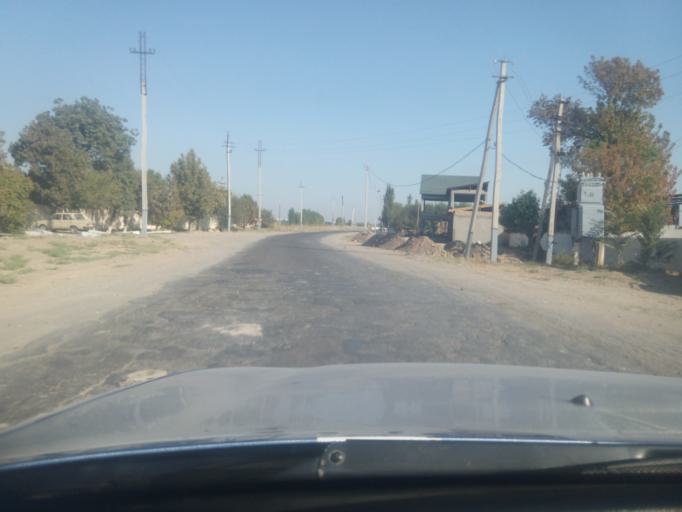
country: UZ
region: Sirdaryo
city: Guliston
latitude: 40.4958
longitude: 68.8002
